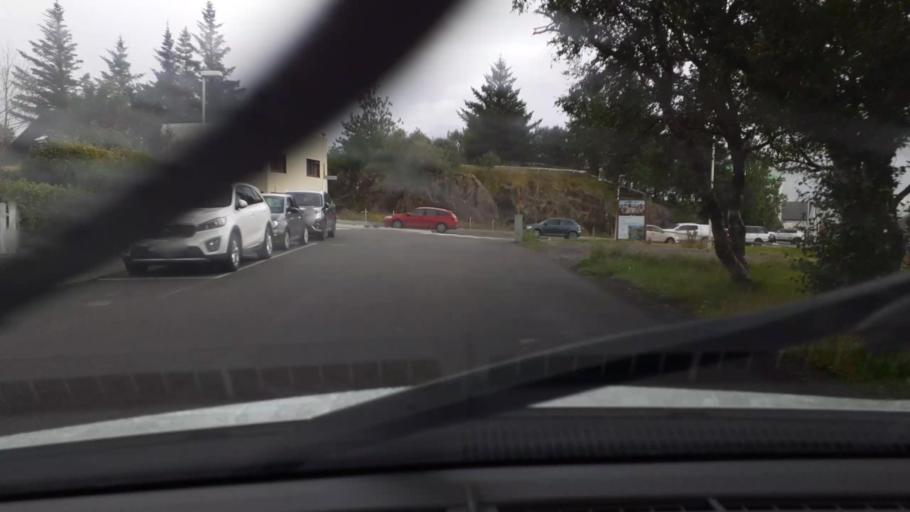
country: IS
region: West
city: Borgarnes
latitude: 64.5380
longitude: -21.9262
